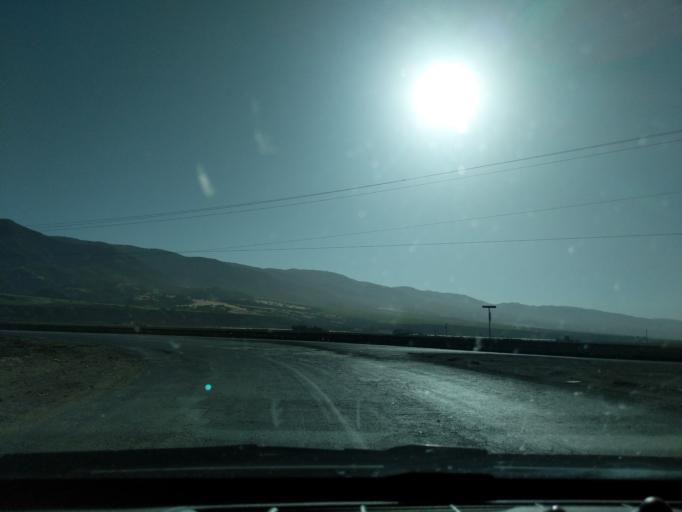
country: US
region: California
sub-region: Monterey County
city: Soledad
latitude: 36.4075
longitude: -121.3578
